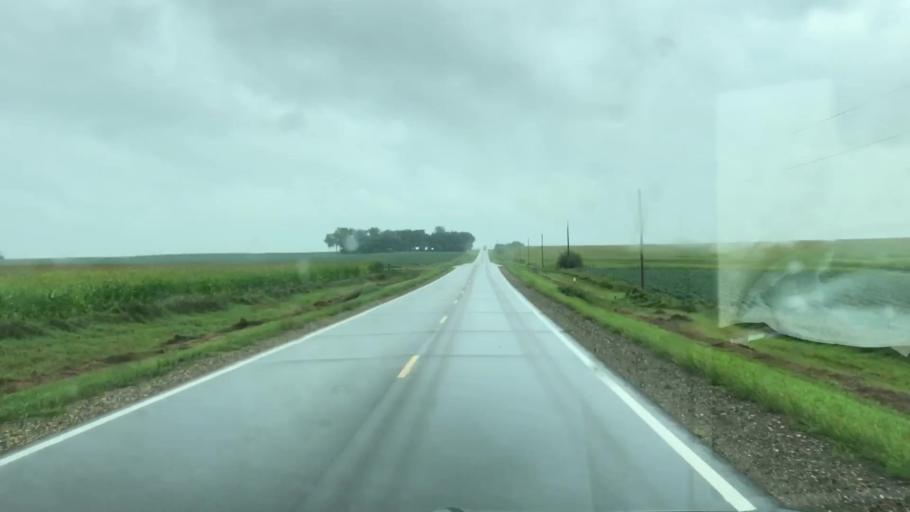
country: US
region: Iowa
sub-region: O'Brien County
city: Sanborn
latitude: 43.2630
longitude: -95.7237
